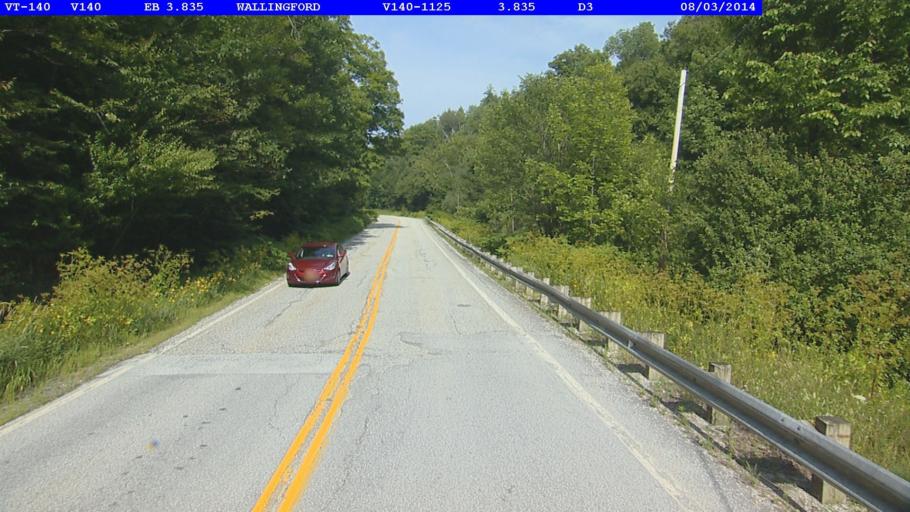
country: US
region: Vermont
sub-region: Rutland County
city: Rutland
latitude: 43.4583
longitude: -72.9138
